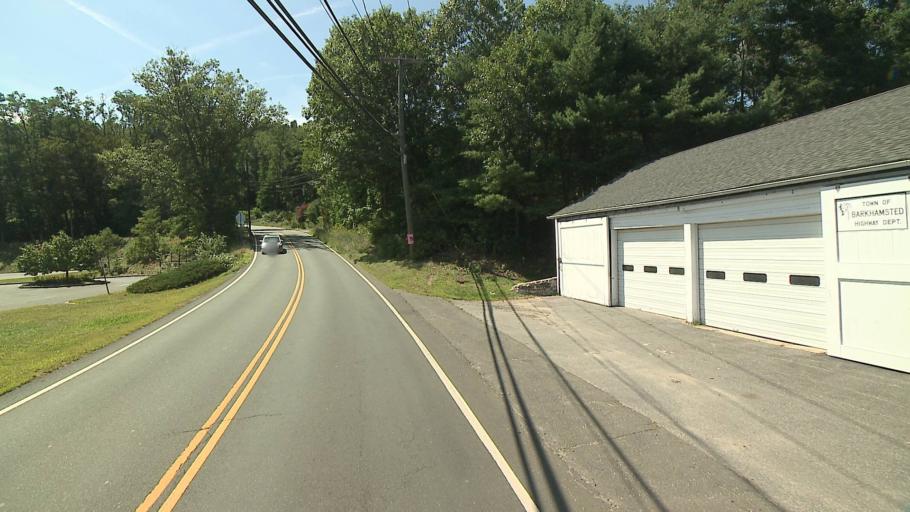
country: US
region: Connecticut
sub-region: Litchfield County
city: New Hartford Center
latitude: 41.9121
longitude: -72.9898
